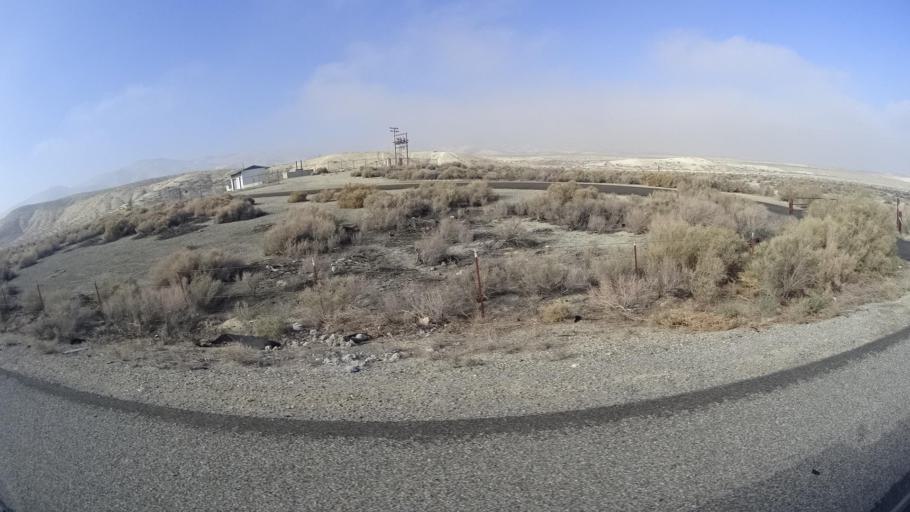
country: US
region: California
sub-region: Kern County
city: Maricopa
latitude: 35.0421
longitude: -119.4256
